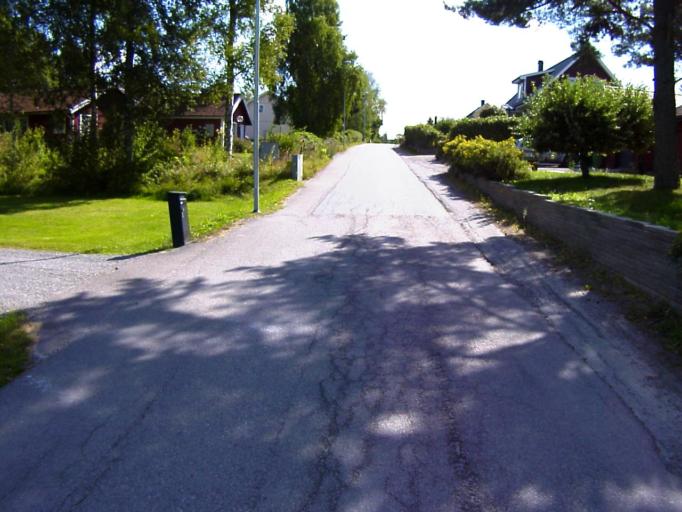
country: SE
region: Soedermanland
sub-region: Eskilstuna Kommun
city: Eskilstuna
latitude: 59.3526
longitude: 16.5569
